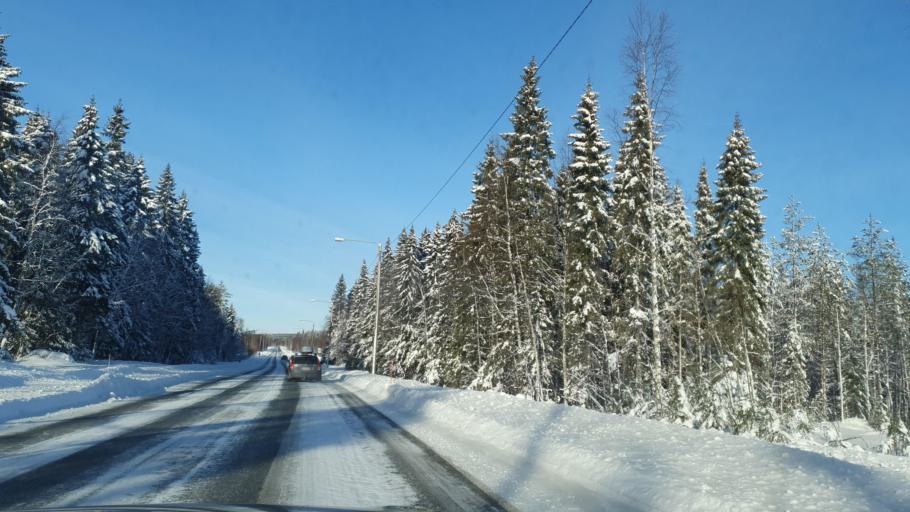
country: FI
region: Lapland
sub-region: Torniolaakso
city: Ylitornio
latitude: 66.1509
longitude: 23.9386
